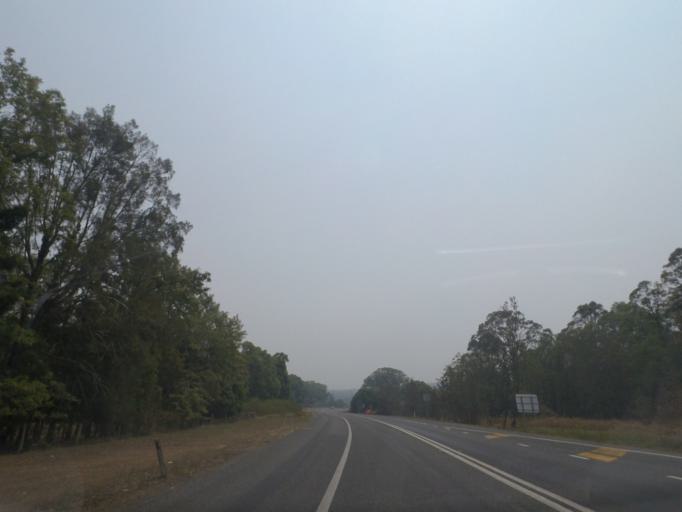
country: AU
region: New South Wales
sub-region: Clarence Valley
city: Maclean
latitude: -29.5477
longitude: 153.1561
